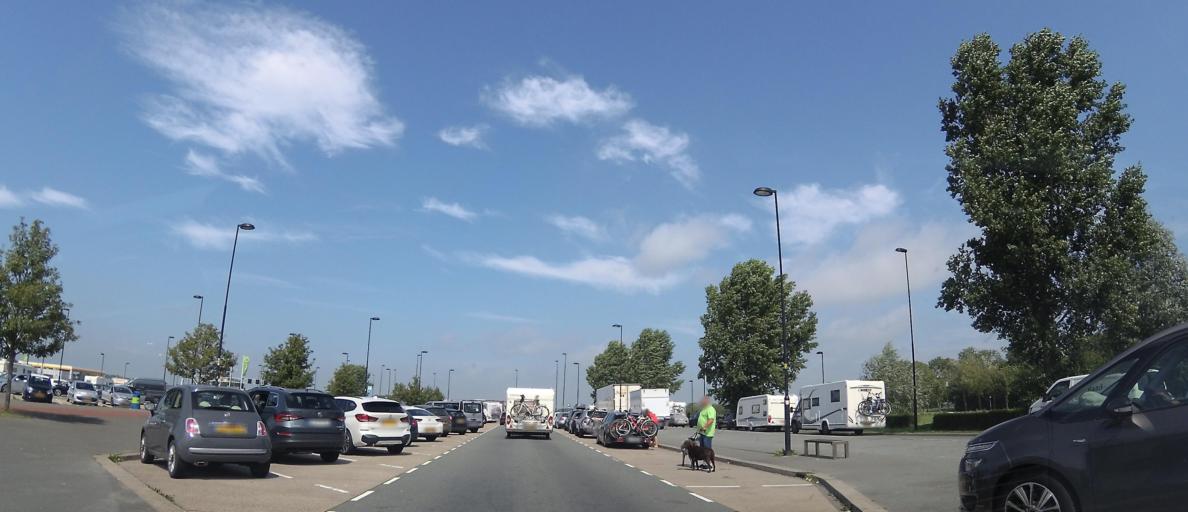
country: NL
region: Gelderland
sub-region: Gemeente Maasdriel
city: Hedel
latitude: 51.7754
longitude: 5.2610
